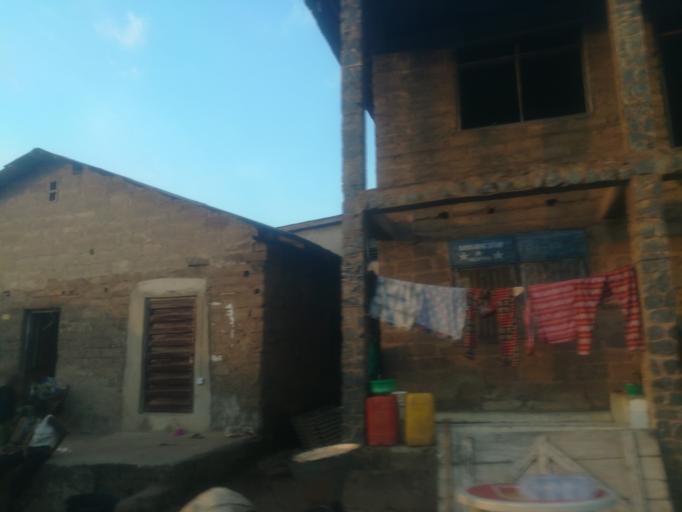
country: NG
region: Ogun
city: Abeokuta
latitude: 7.1495
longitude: 3.3313
